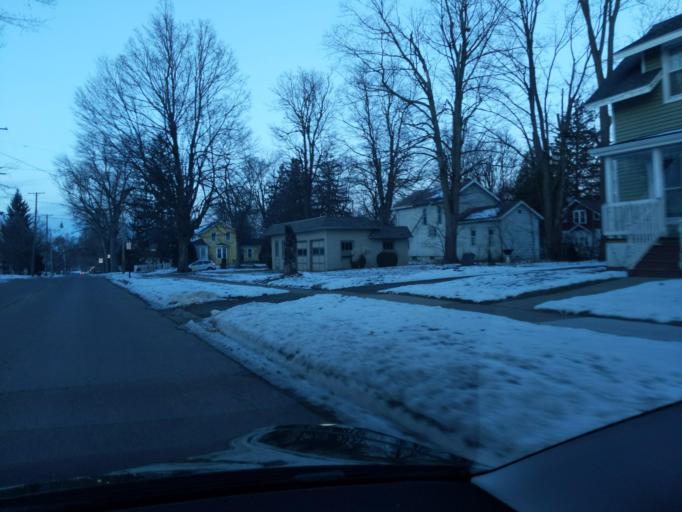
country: US
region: Michigan
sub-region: Ingham County
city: Mason
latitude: 42.5765
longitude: -84.4479
